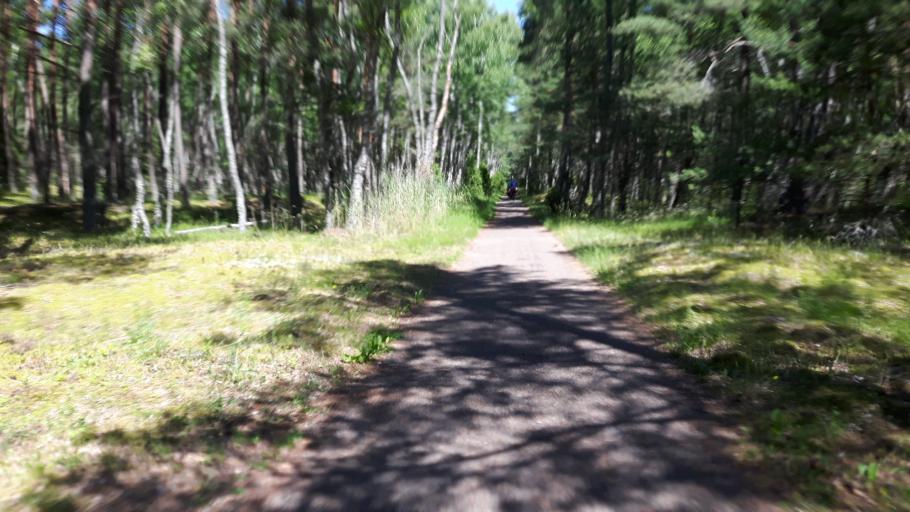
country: LT
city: Neringa
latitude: 55.4275
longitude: 21.0759
